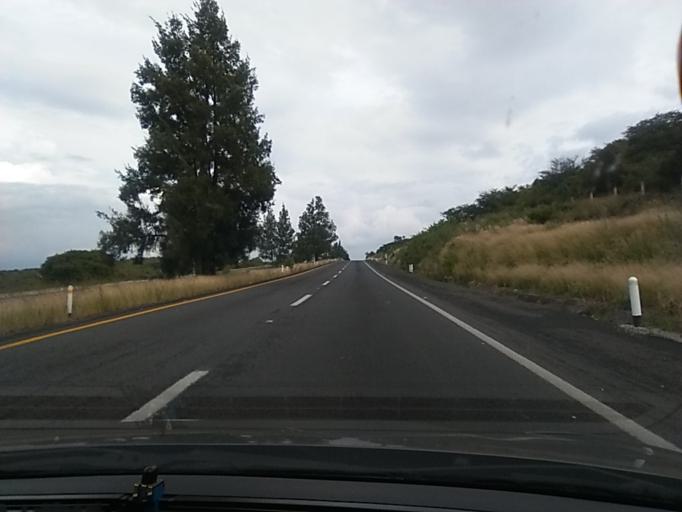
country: MX
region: Michoacan
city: Ixtlan
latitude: 20.2032
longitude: -102.3342
